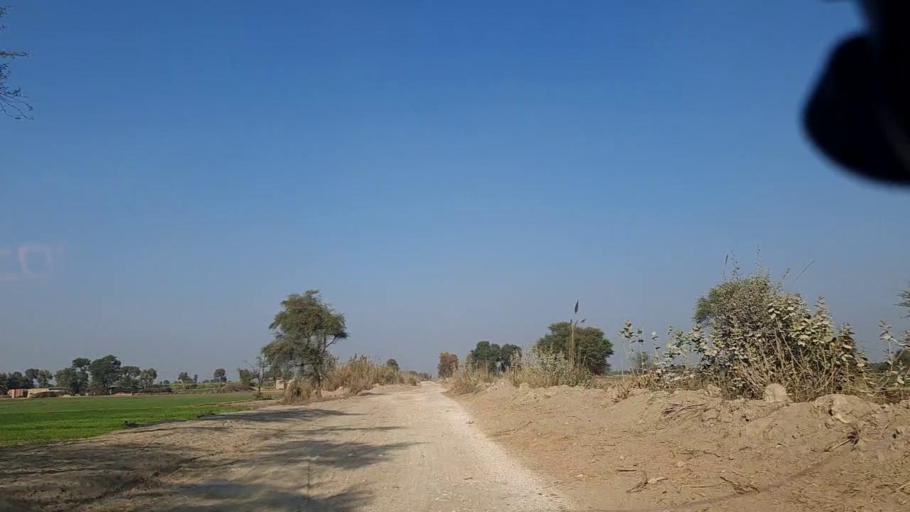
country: PK
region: Sindh
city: Khanpur
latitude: 27.6887
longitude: 69.4964
